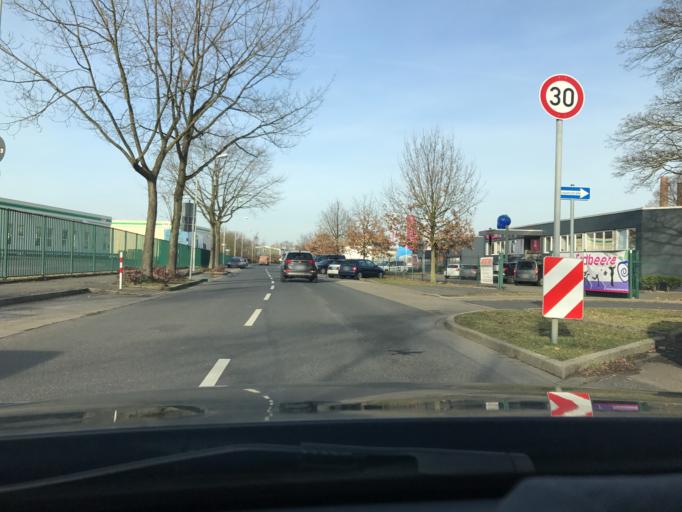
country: DE
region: North Rhine-Westphalia
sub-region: Regierungsbezirk Dusseldorf
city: Krefeld
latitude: 51.3431
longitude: 6.5398
